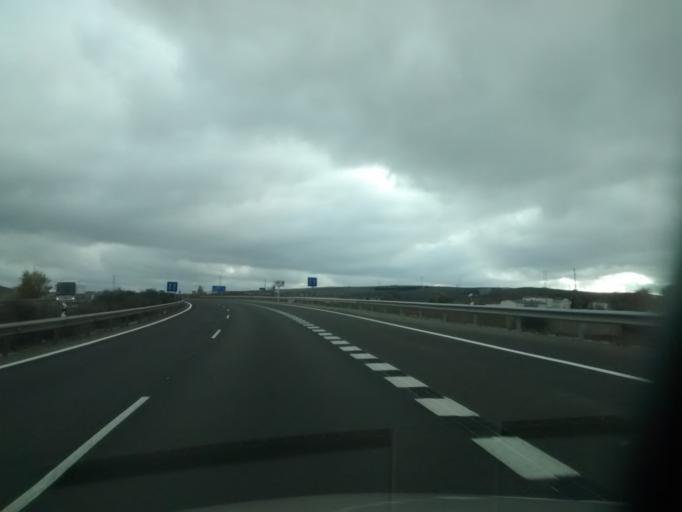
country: ES
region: Castille-La Mancha
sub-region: Provincia de Guadalajara
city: Torremocha del Campo
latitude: 40.9814
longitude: -2.6137
